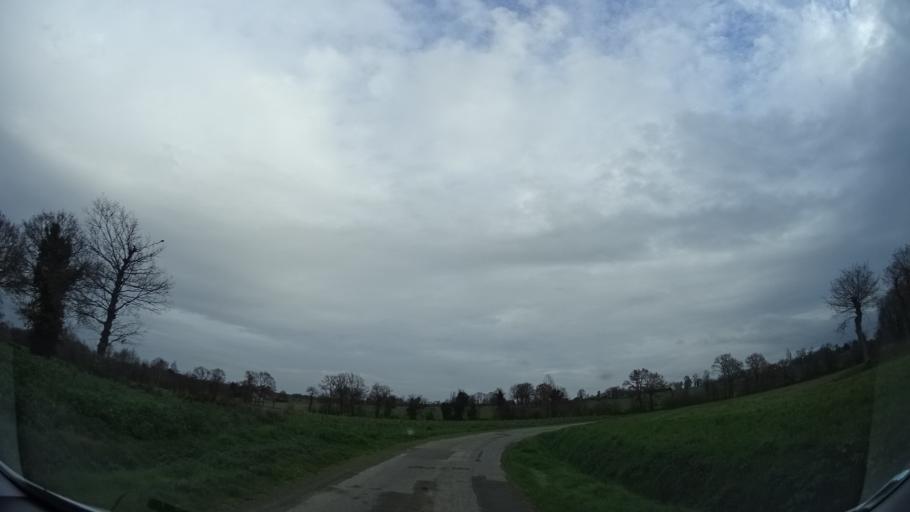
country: FR
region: Brittany
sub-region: Departement des Cotes-d'Armor
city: Evran
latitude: 48.3357
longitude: -1.9554
